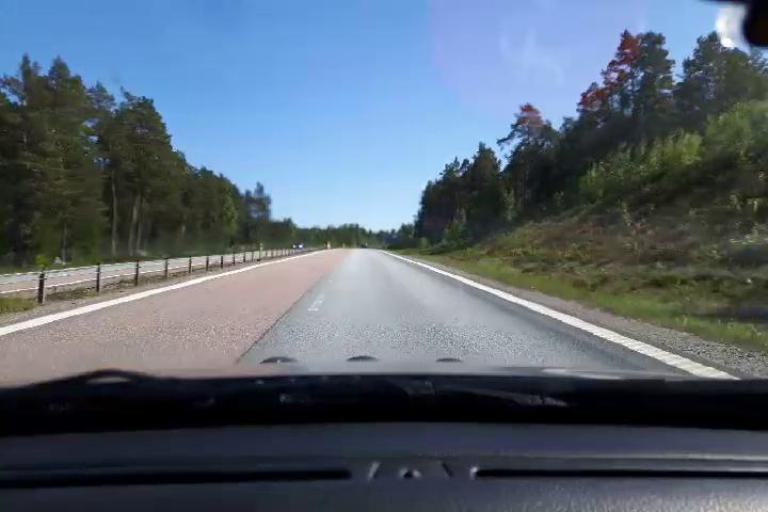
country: SE
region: Gaevleborg
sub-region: Soderhamns Kommun
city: Soderhamn
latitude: 61.3234
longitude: 17.0299
